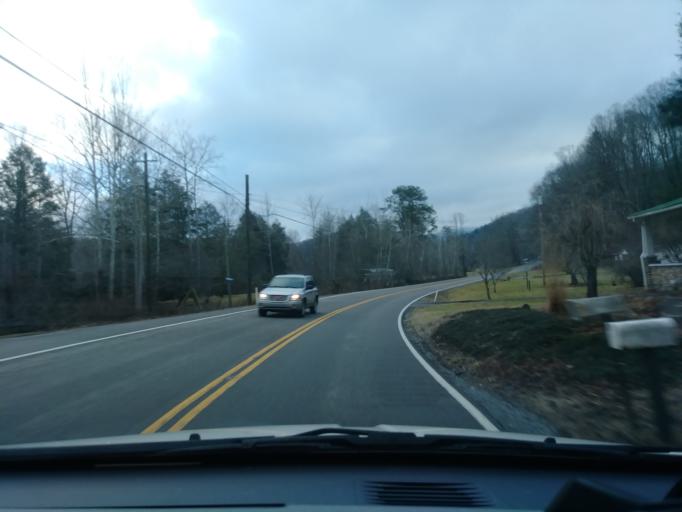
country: US
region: Tennessee
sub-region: Unicoi County
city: Unicoi
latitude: 36.1765
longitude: -82.2953
